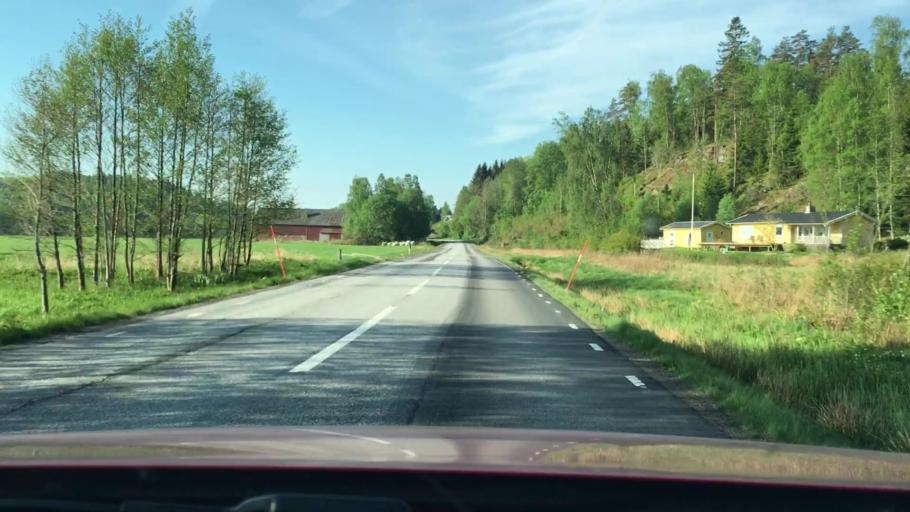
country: SE
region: Vaestra Goetaland
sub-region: Munkedals Kommun
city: Munkedal
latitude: 58.6240
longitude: 11.5598
